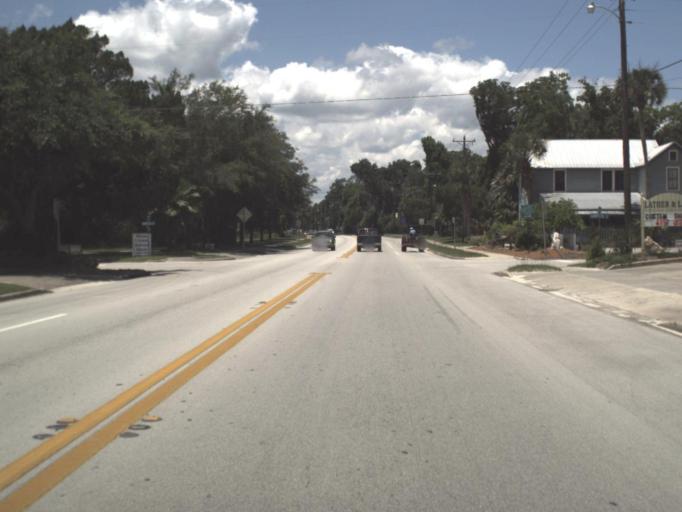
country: US
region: Florida
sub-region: Clay County
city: Keystone Heights
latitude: 29.7098
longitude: -82.0505
